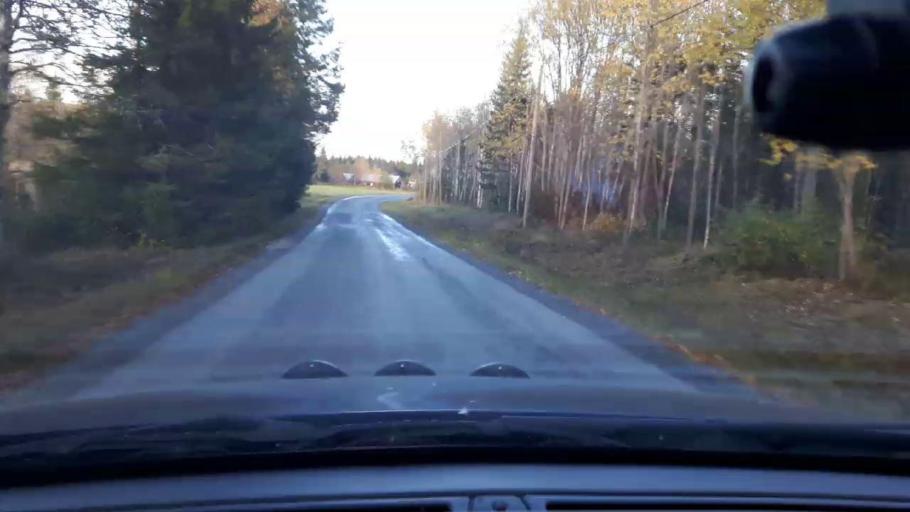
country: SE
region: Jaemtland
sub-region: Bergs Kommun
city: Hoverberg
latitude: 63.0625
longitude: 14.2585
